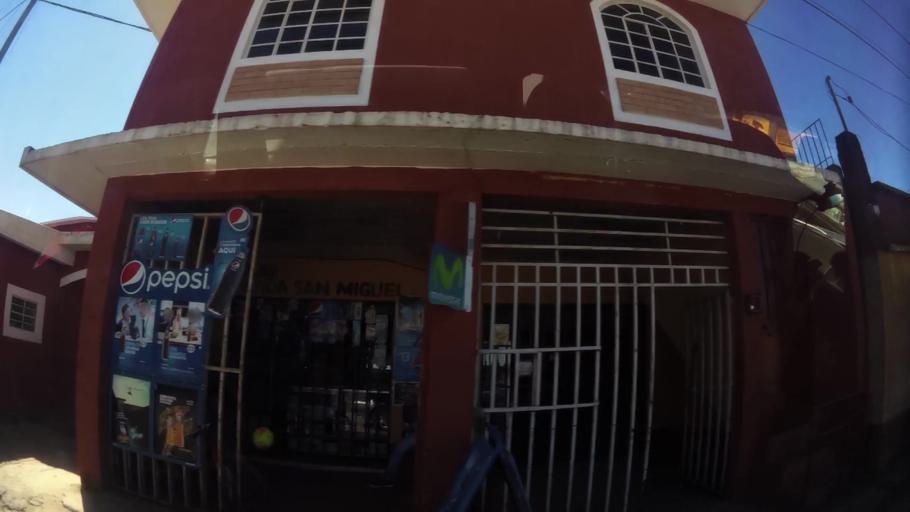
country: GT
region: Guatemala
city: San Jose Pinula
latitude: 14.5278
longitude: -90.4157
